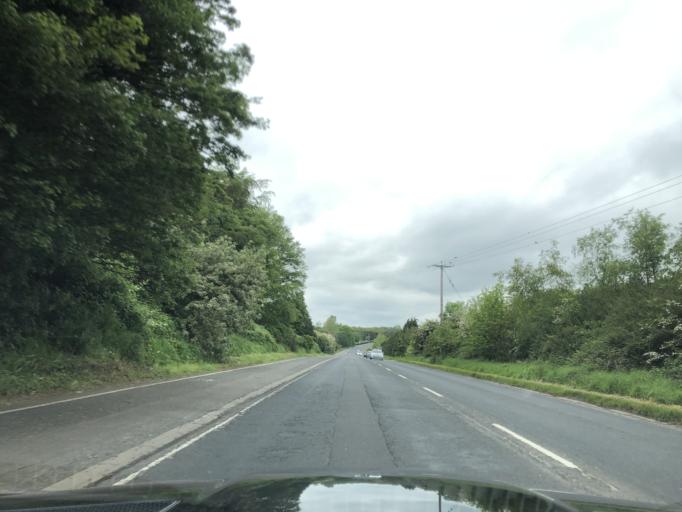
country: GB
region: Northern Ireland
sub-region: Down District
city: Downpatrick
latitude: 54.3389
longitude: -5.7262
